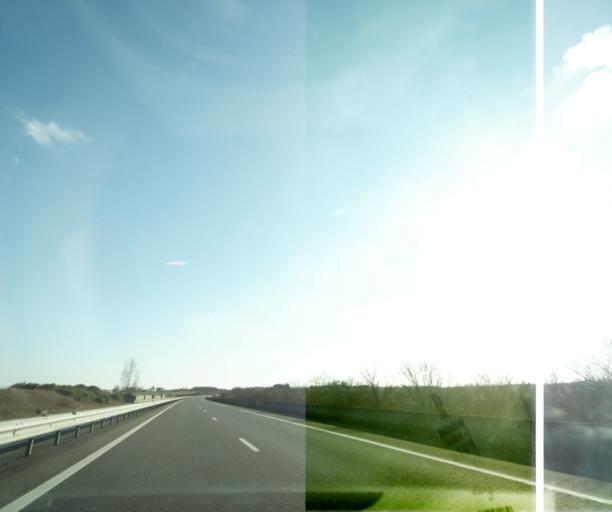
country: FR
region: Midi-Pyrenees
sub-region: Departement du Tarn-et-Garonne
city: Caussade
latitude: 44.2142
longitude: 1.5407
